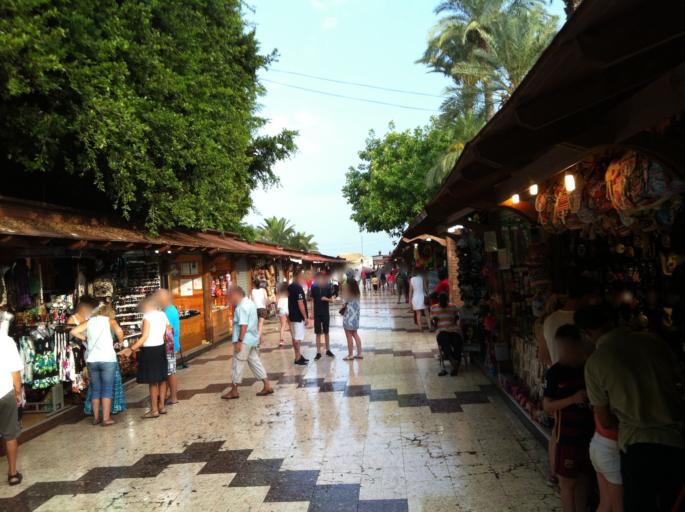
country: ES
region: Valencia
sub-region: Provincia de Alicante
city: Torrevieja
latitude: 37.9747
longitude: -0.6790
